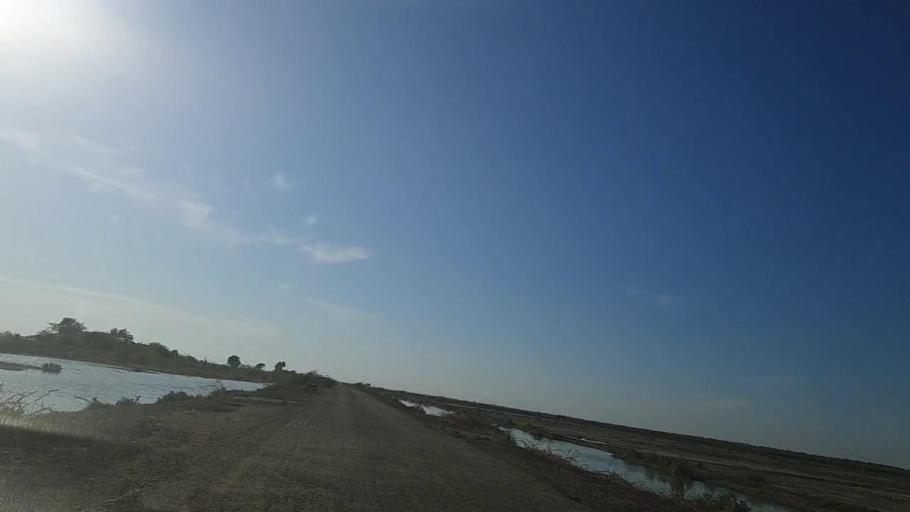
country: PK
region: Sindh
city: Pithoro
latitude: 25.5091
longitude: 69.4380
